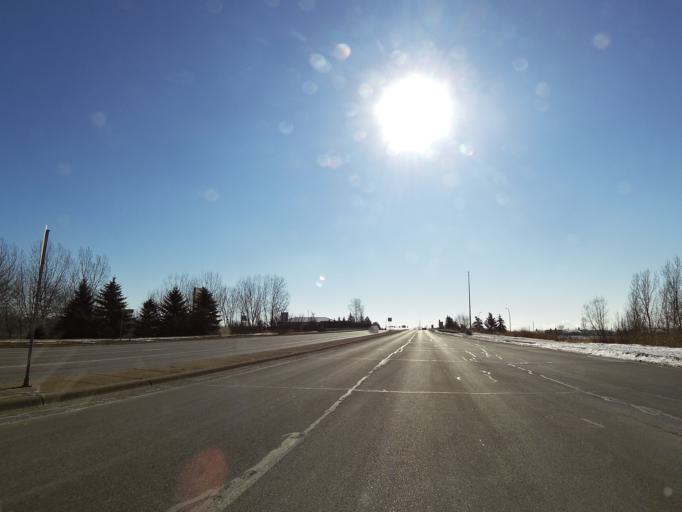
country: US
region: Minnesota
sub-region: Washington County
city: Woodbury
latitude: 44.9172
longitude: -92.9810
